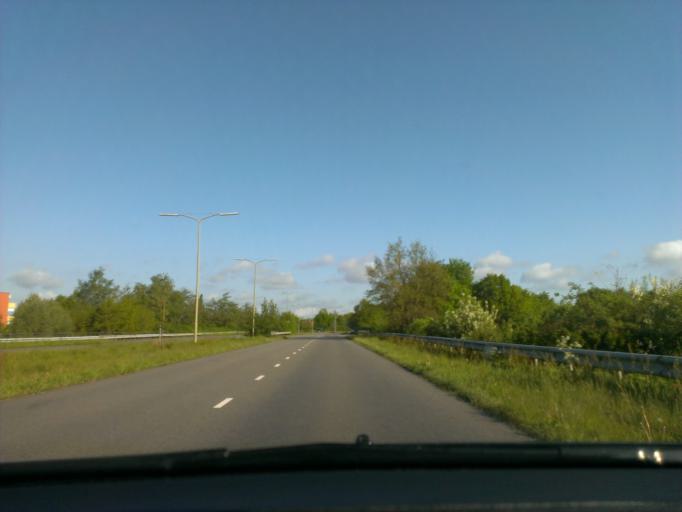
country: NL
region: Drenthe
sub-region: Gemeente Emmen
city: Emmen
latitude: 52.7640
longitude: 6.8979
